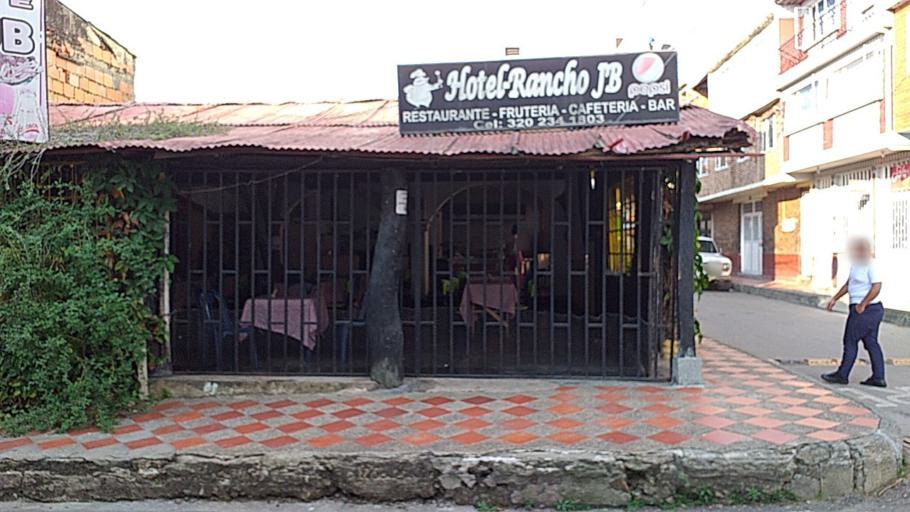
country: CO
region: Boyaca
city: Santana
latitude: 6.0580
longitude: -73.4824
